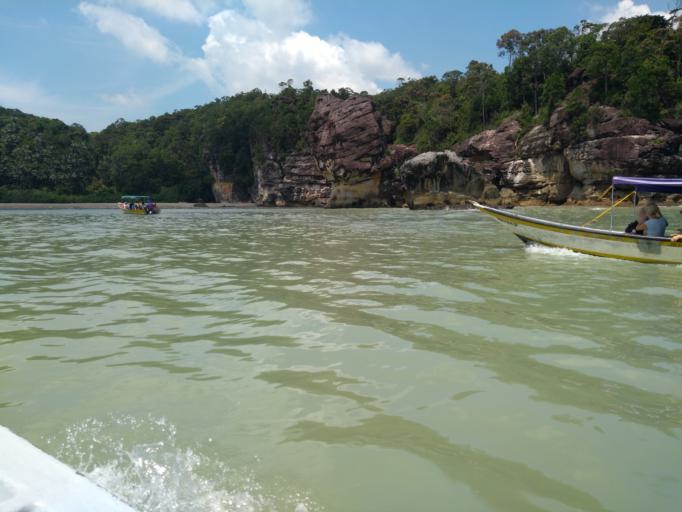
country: MY
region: Sarawak
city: Kuching
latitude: 1.7311
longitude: 110.4454
